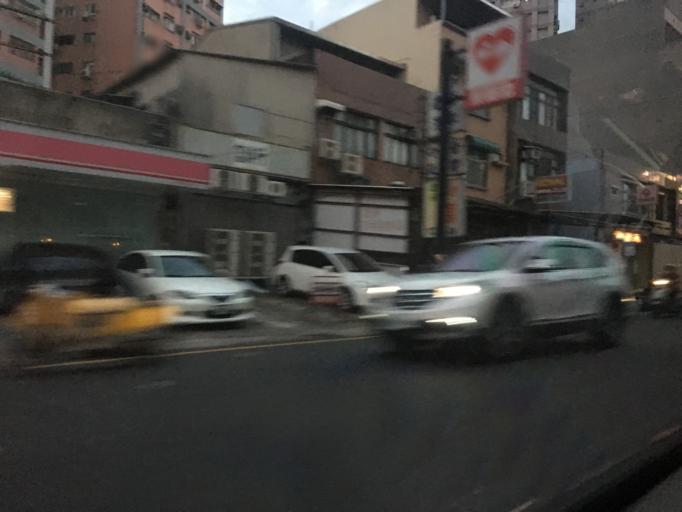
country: TW
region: Taiwan
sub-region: Hsinchu
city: Hsinchu
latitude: 24.7968
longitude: 120.9612
